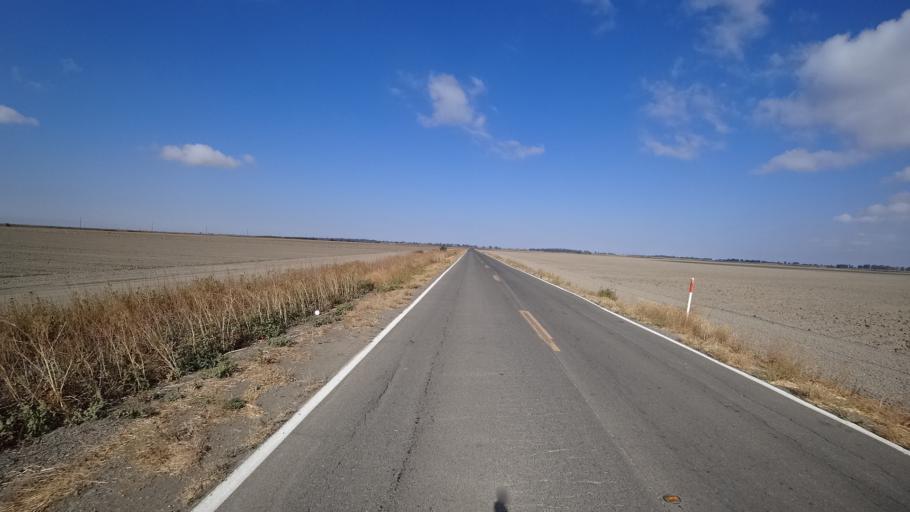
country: US
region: California
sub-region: Yolo County
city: Woodland
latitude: 38.8291
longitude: -121.7488
